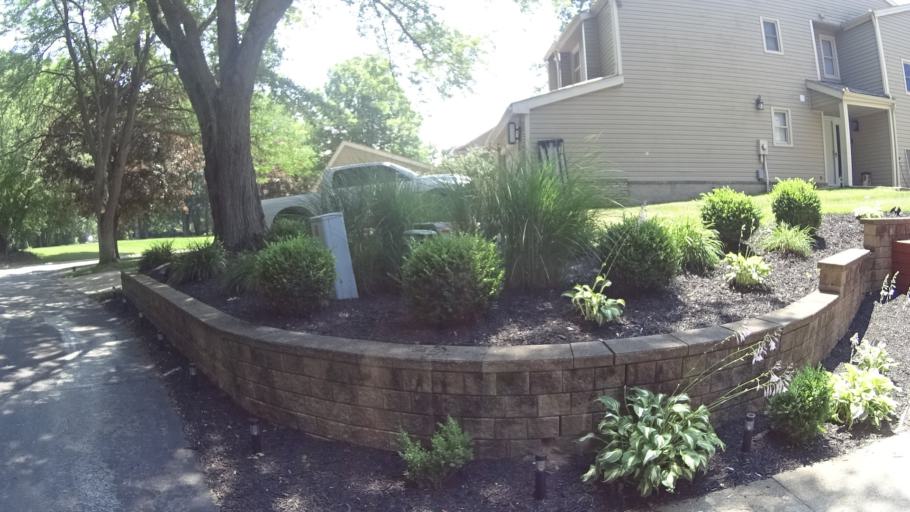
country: US
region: Ohio
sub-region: Erie County
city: Sandusky
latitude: 41.4126
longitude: -82.6384
